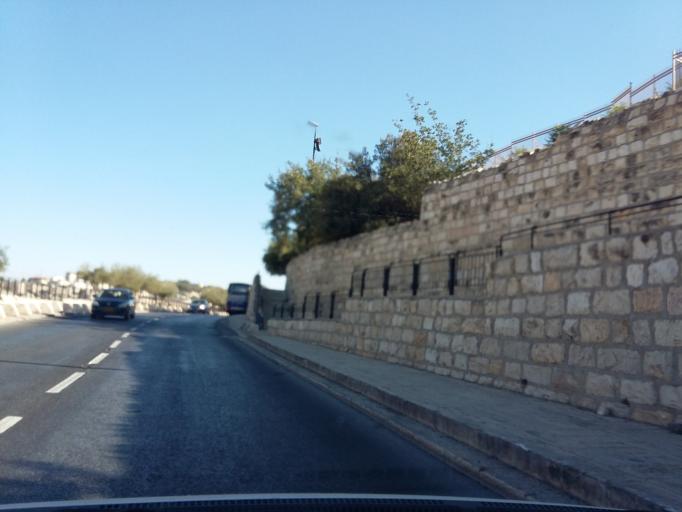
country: PS
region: West Bank
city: Old City
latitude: 31.7788
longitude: 35.2379
